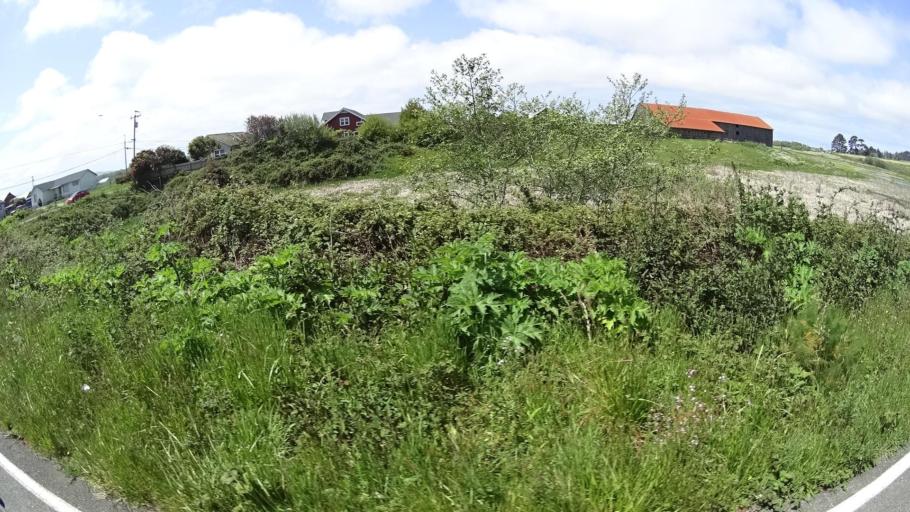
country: US
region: California
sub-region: Humboldt County
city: Ferndale
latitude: 40.6432
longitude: -124.2264
